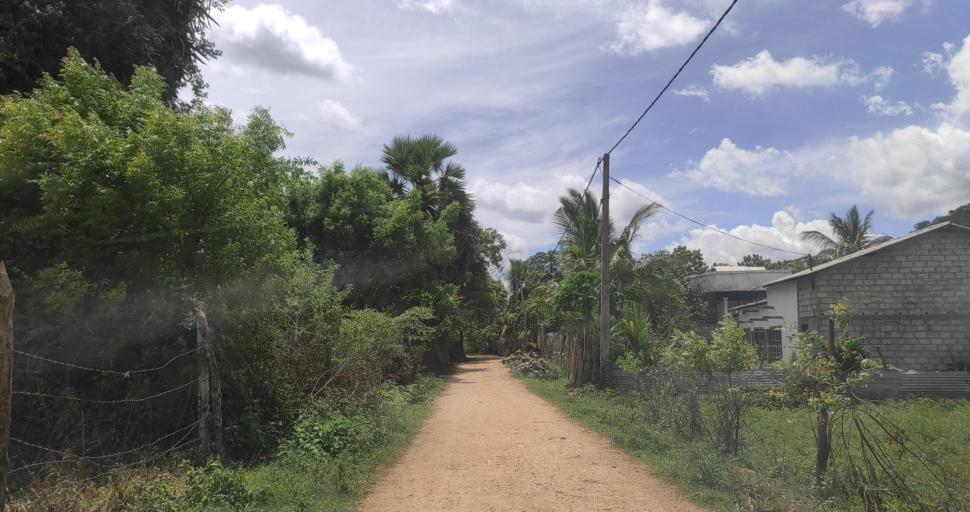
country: LK
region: Eastern Province
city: Trincomalee
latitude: 8.4425
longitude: 81.0493
